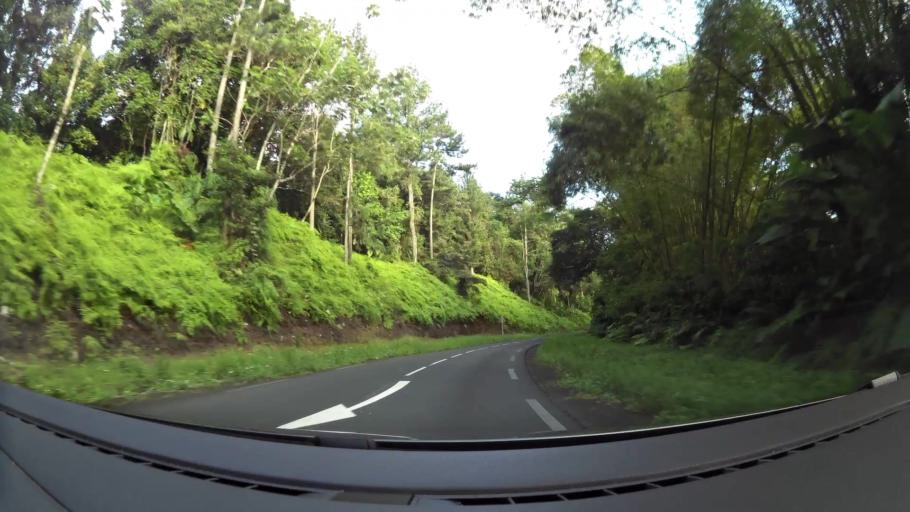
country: GP
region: Guadeloupe
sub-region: Guadeloupe
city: Bouillante
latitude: 16.1803
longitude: -61.7138
